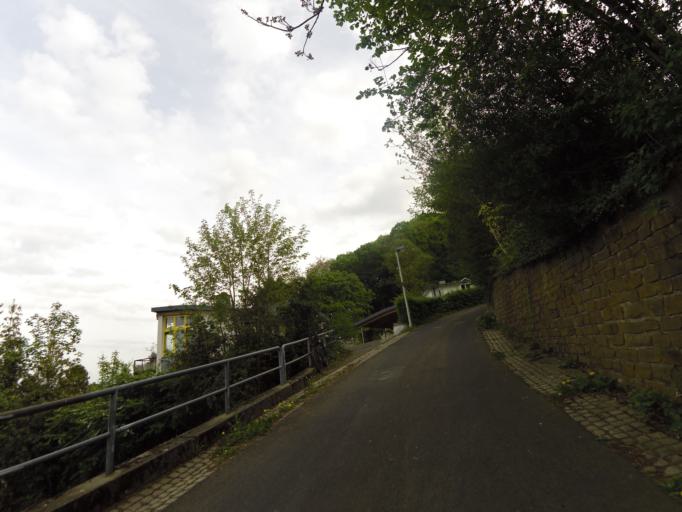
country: DE
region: North Rhine-Westphalia
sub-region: Regierungsbezirk Koln
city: Bonn
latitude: 50.6996
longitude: 7.1112
